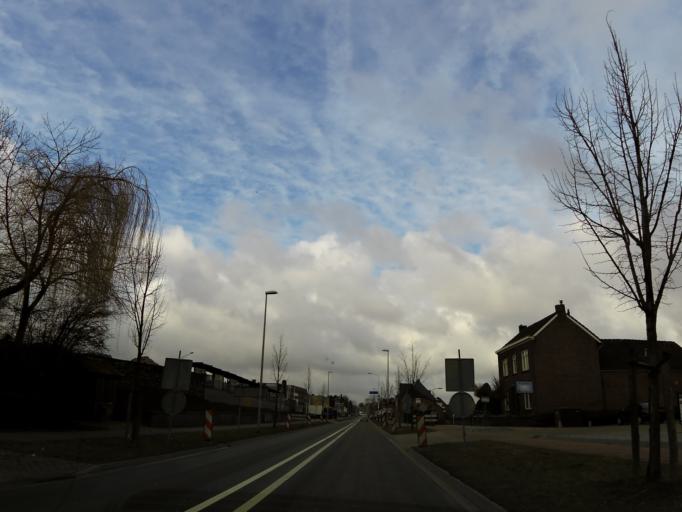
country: NL
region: Limburg
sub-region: Eijsden-Margraten
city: Margraten
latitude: 50.8170
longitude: 5.8334
